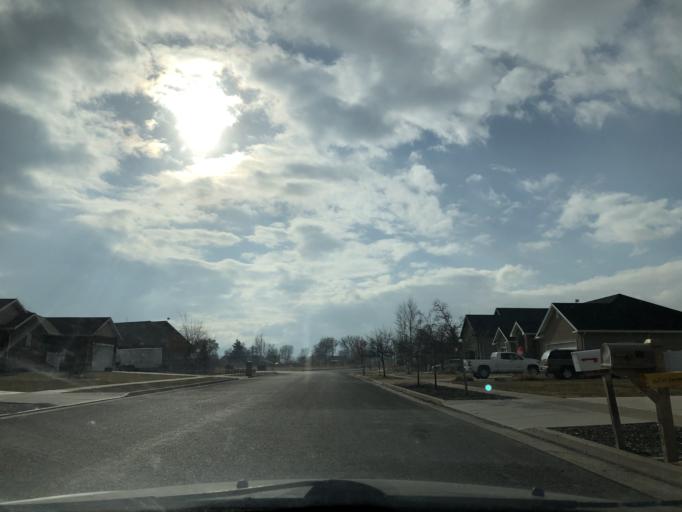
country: US
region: Utah
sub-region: Cache County
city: Wellsville
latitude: 41.6513
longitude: -111.9114
